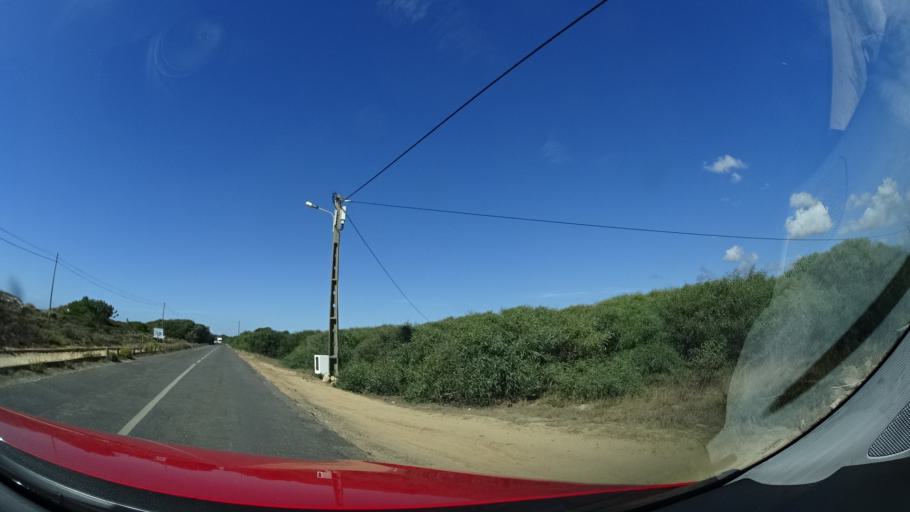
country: PT
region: Beja
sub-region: Odemira
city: Sao Teotonio
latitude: 37.5328
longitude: -8.7844
